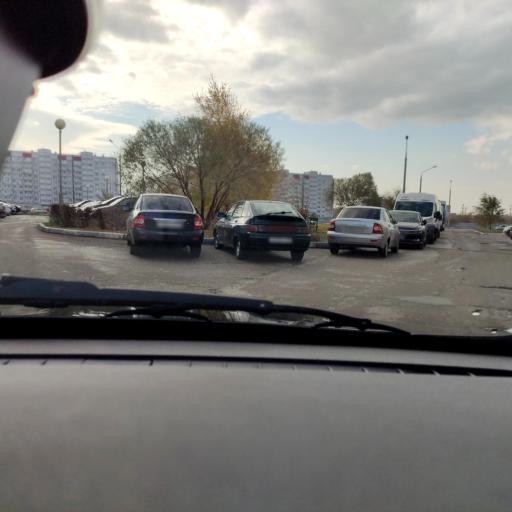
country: RU
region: Samara
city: Tol'yatti
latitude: 53.5279
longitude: 49.3376
